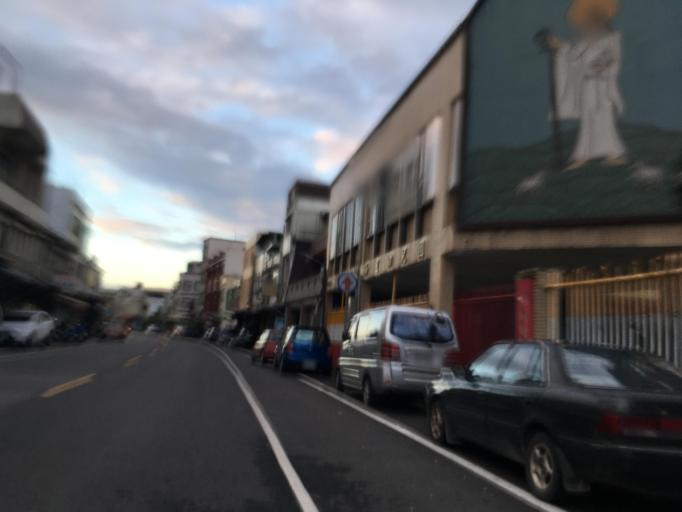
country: TW
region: Taiwan
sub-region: Yilan
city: Yilan
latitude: 24.6226
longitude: 121.8344
